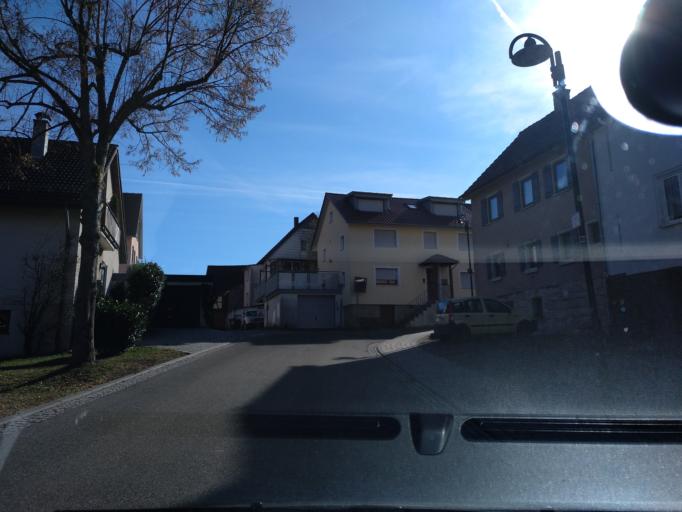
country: DE
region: Baden-Wuerttemberg
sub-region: Regierungsbezirk Stuttgart
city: Mainhardt
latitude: 49.1202
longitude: 9.5216
